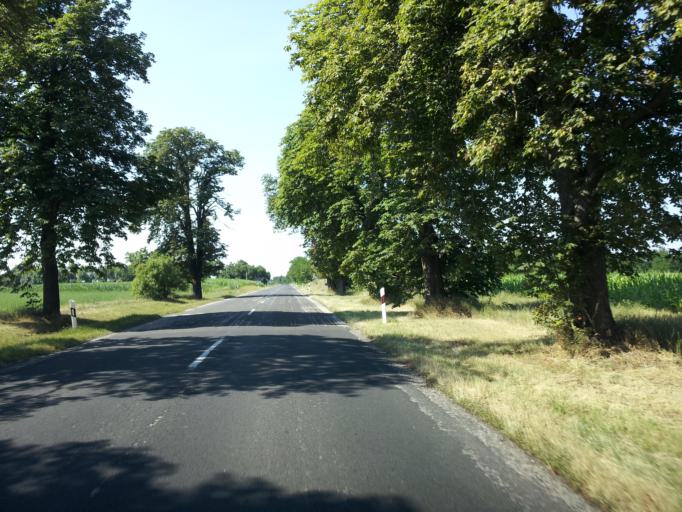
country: HU
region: Fejer
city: Lovasbereny
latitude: 47.2884
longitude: 18.5304
